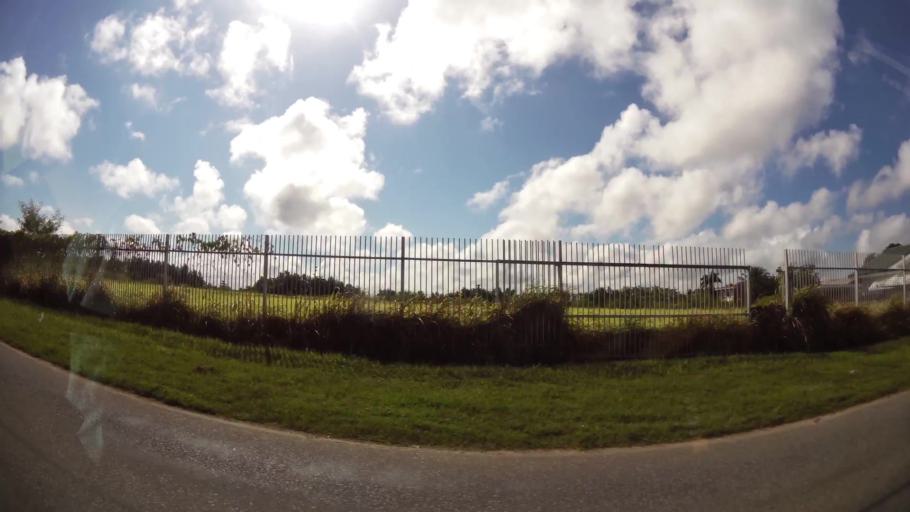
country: SR
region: Commewijne
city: Nieuw Amsterdam
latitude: 5.8644
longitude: -55.1012
